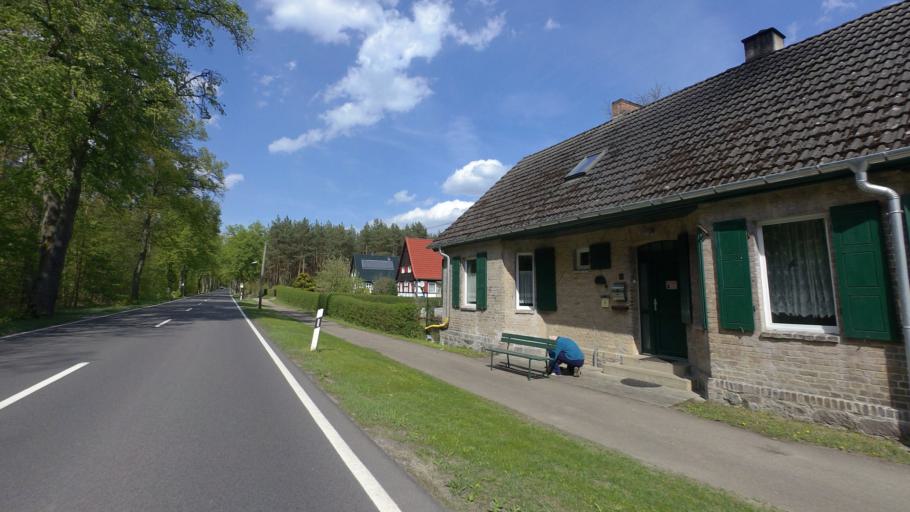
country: DE
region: Brandenburg
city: Milmersdorf
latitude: 53.0406
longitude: 13.6035
